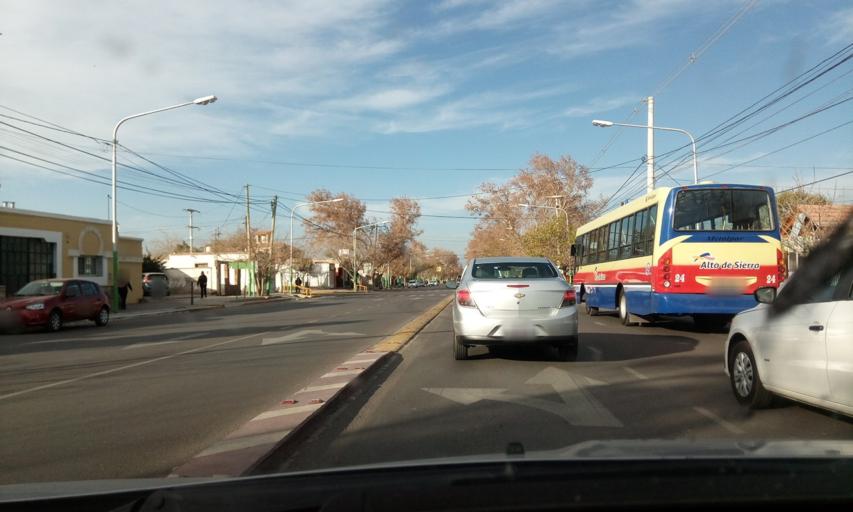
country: AR
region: San Juan
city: San Juan
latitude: -31.5299
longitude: -68.5905
